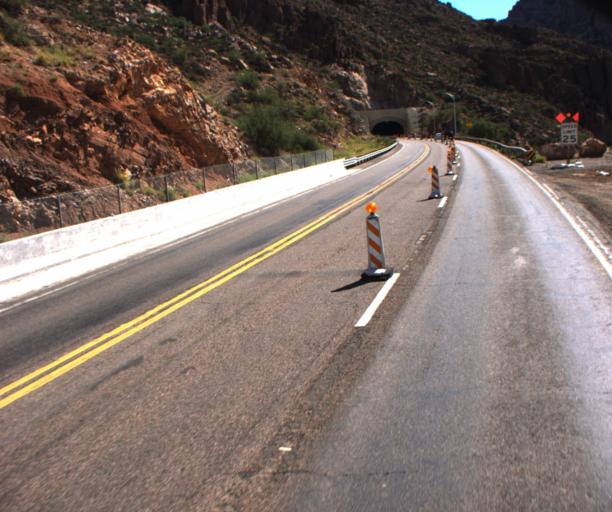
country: US
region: Arizona
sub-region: Pinal County
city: Superior
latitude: 33.3037
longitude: -111.0860
